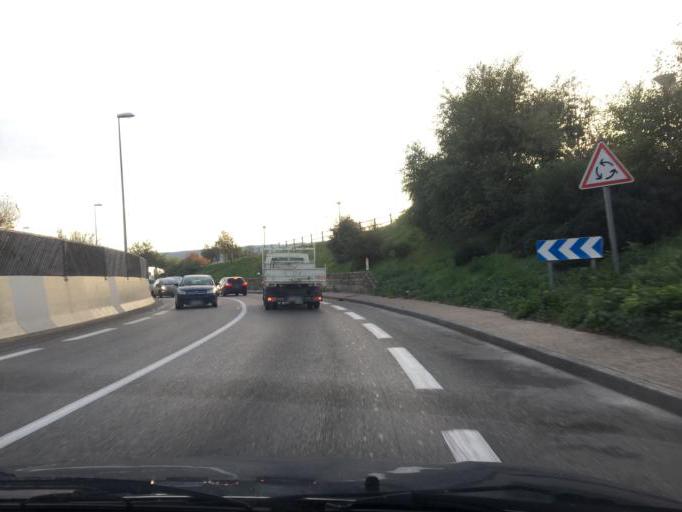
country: FR
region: Provence-Alpes-Cote d'Azur
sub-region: Departement du Vaucluse
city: Cavaillon
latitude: 43.8279
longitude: 5.0320
